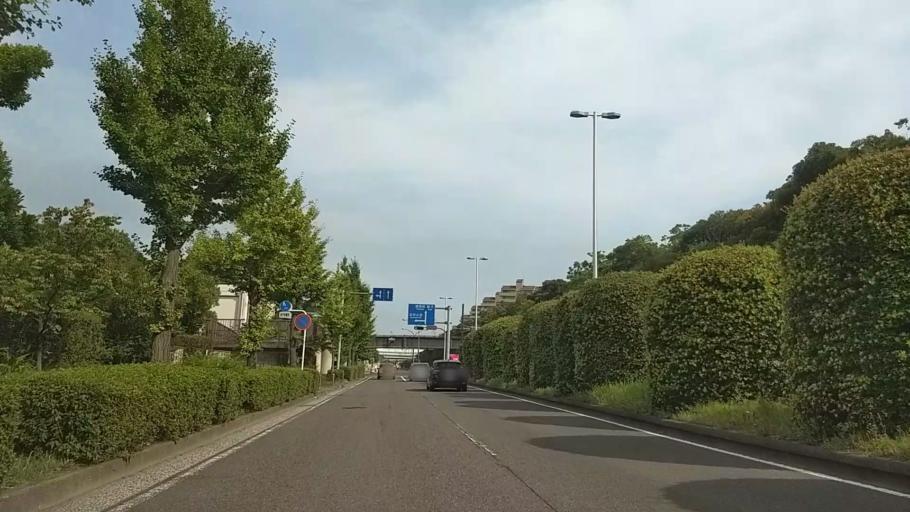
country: JP
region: Kanagawa
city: Yokohama
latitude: 35.4304
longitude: 139.6662
